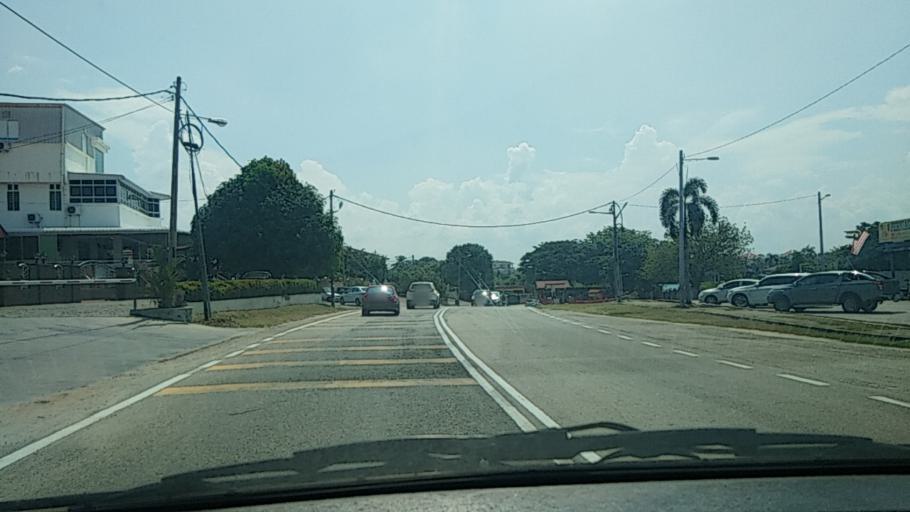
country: MY
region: Kedah
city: Sungai Petani
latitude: 5.6402
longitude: 100.5018
